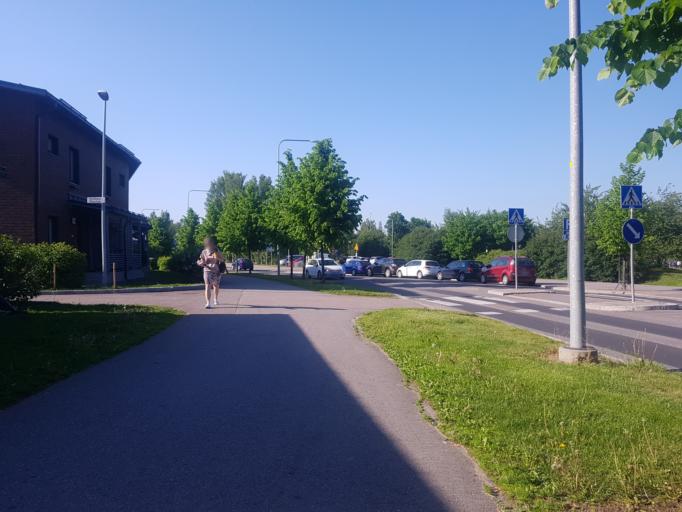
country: FI
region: Uusimaa
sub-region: Helsinki
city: Vantaa
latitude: 60.2662
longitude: 25.0152
